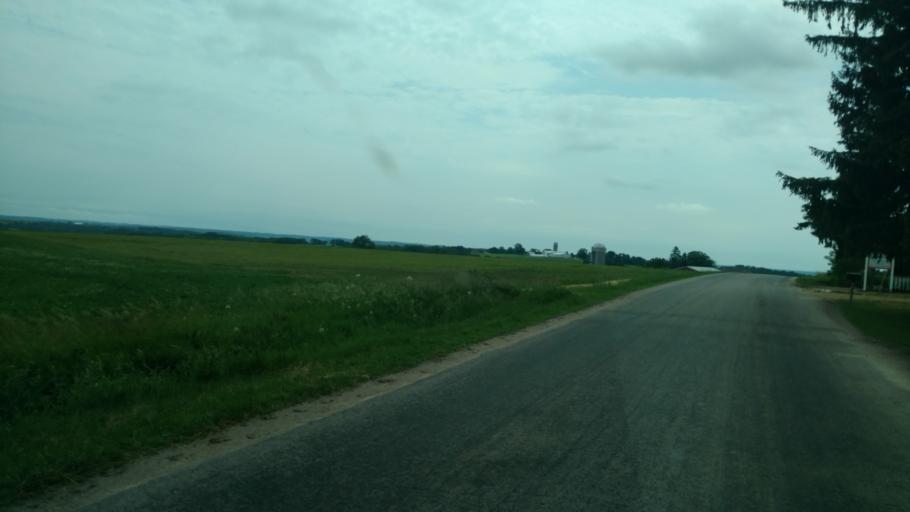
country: US
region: Wisconsin
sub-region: Monroe County
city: Cashton
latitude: 43.7687
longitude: -90.6559
